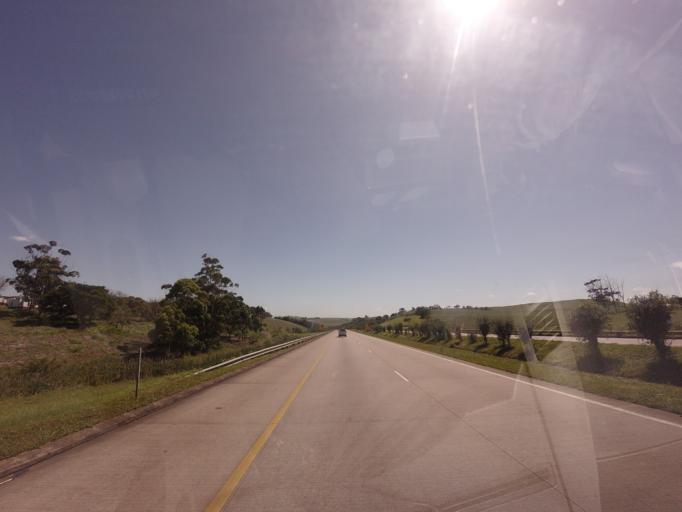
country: ZA
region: KwaZulu-Natal
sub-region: iLembe District Municipality
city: Ballitoville
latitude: -29.4600
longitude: 31.2458
